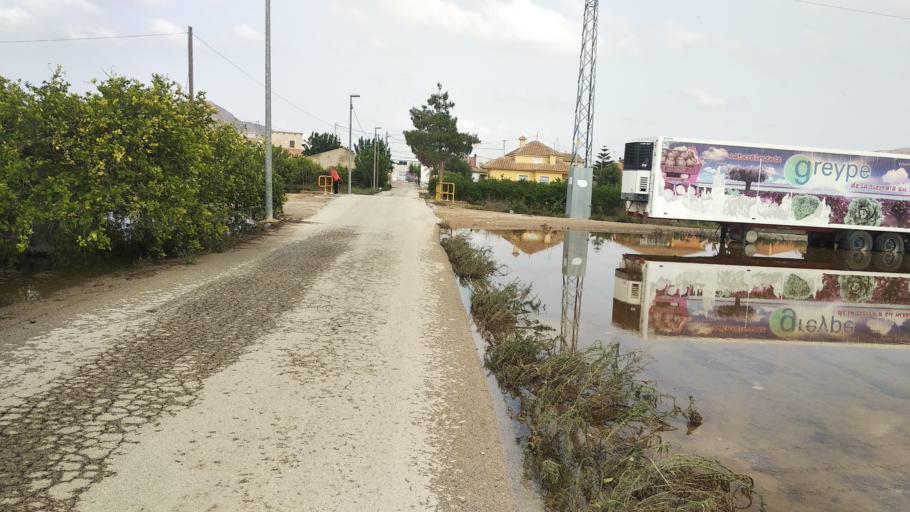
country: ES
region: Murcia
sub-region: Murcia
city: Santomera
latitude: 38.0417
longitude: -1.0412
